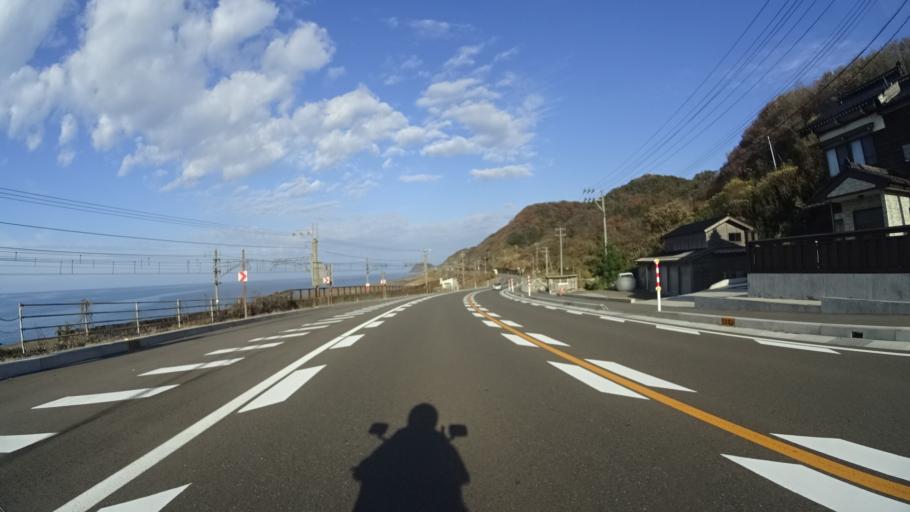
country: JP
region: Niigata
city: Kashiwazaki
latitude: 37.2967
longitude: 138.4077
